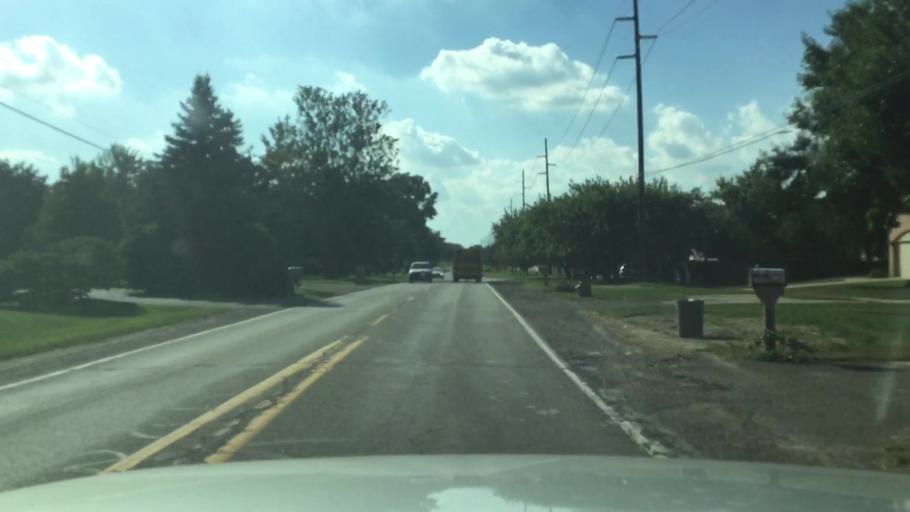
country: US
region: Michigan
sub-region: Wayne County
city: Westland
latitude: 42.3527
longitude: -83.4225
